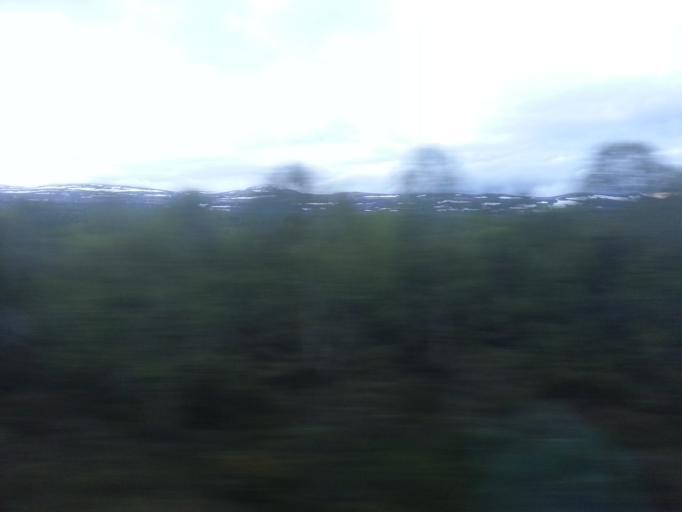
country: NO
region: Oppland
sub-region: Dovre
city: Dombas
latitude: 62.1041
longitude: 9.2240
